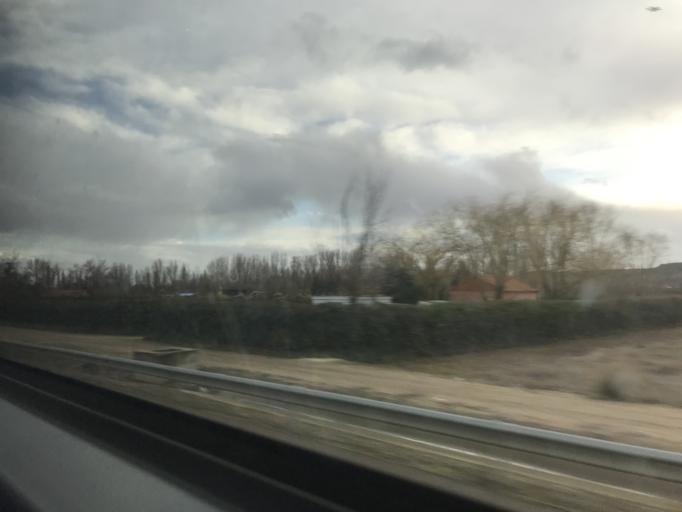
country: ES
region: Castille and Leon
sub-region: Provincia de Palencia
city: Grijota
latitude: 42.0373
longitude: -4.5620
